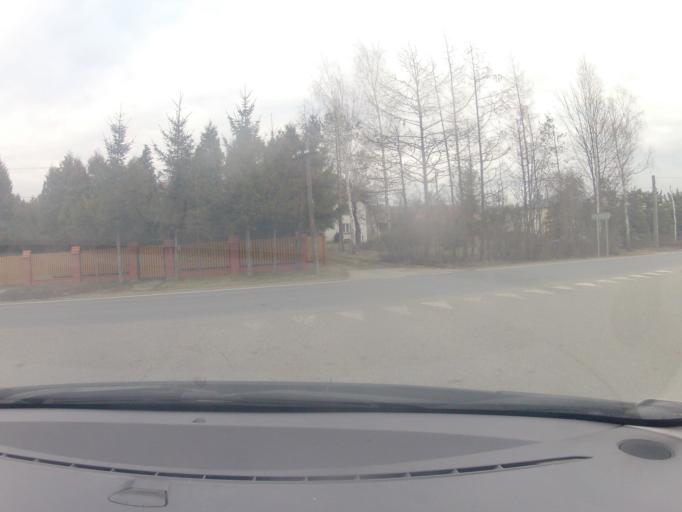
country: PL
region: Subcarpathian Voivodeship
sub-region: Powiat krosnienski
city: Dukla
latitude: 49.5583
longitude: 21.6274
